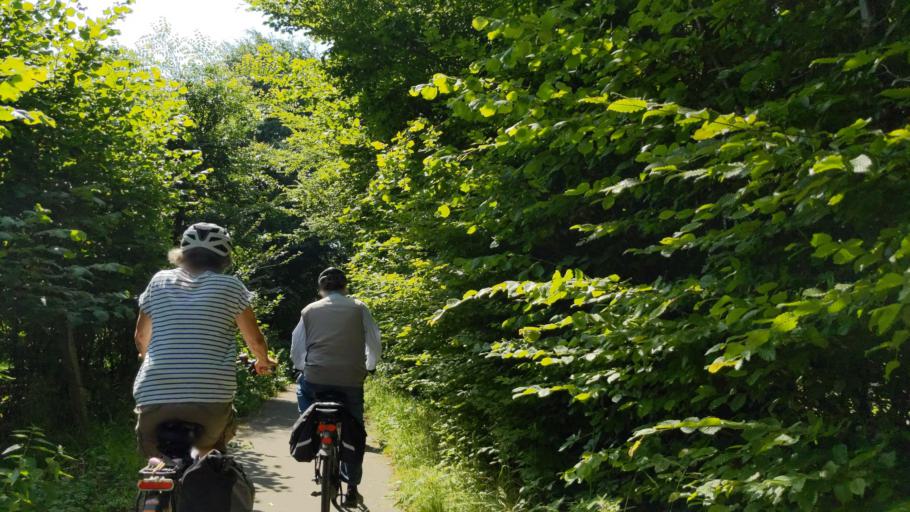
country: DE
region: Schleswig-Holstein
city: Klempau
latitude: 53.7599
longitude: 10.6569
